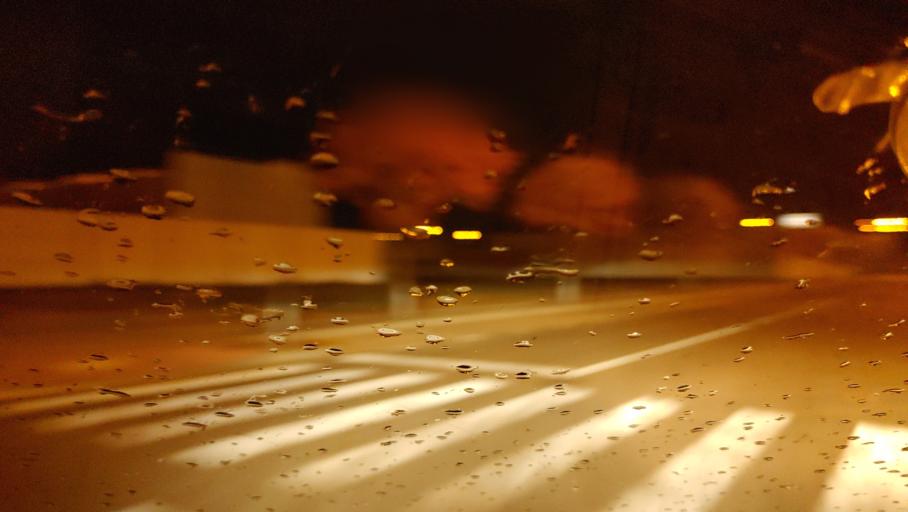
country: ES
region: Castille-La Mancha
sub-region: Provincia de Ciudad Real
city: Ciudad Real
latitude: 38.9843
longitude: -3.9082
